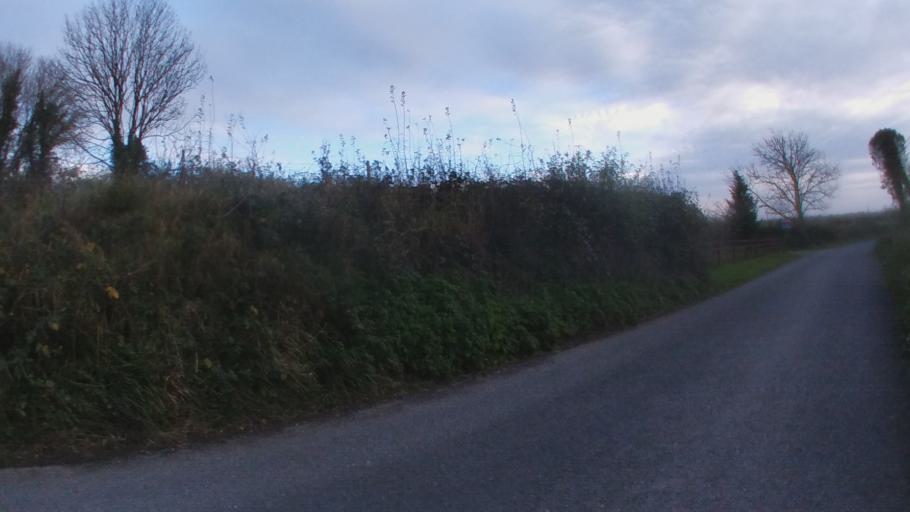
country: IE
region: Leinster
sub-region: Kilkenny
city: Kilkenny
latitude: 52.6875
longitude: -7.1753
